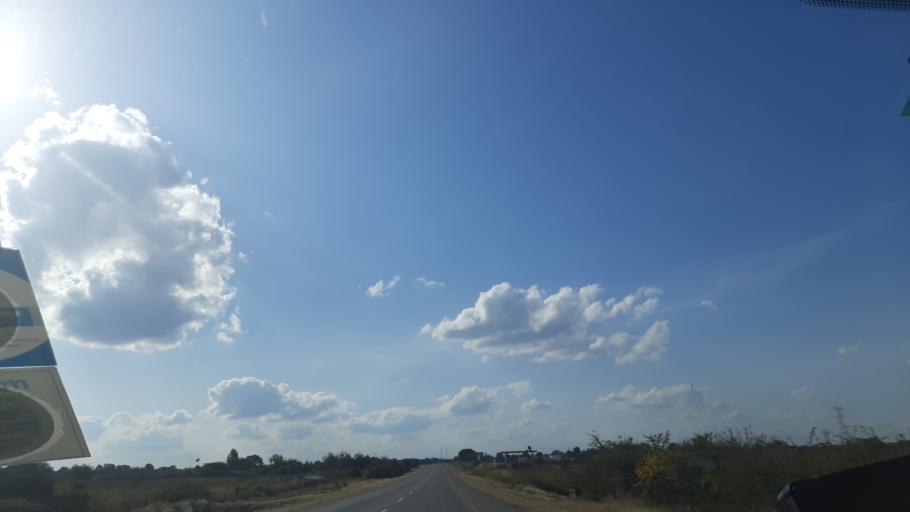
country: TZ
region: Singida
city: Ikungi
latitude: -5.1616
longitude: 34.7785
